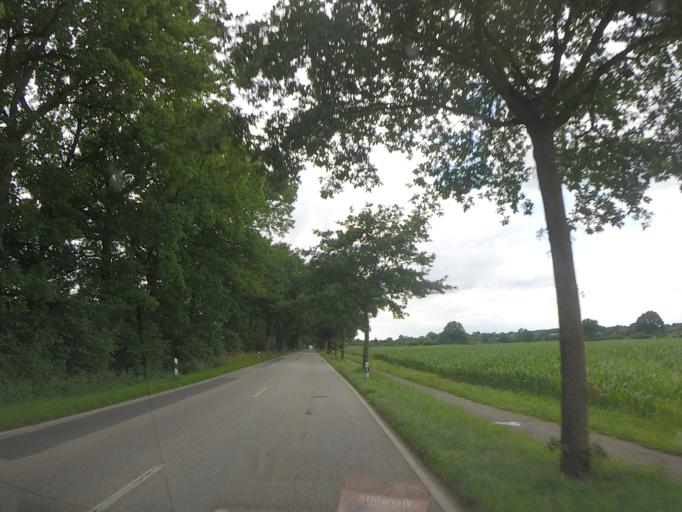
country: DE
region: Schleswig-Holstein
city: Ratekau
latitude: 53.9713
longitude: 10.7176
